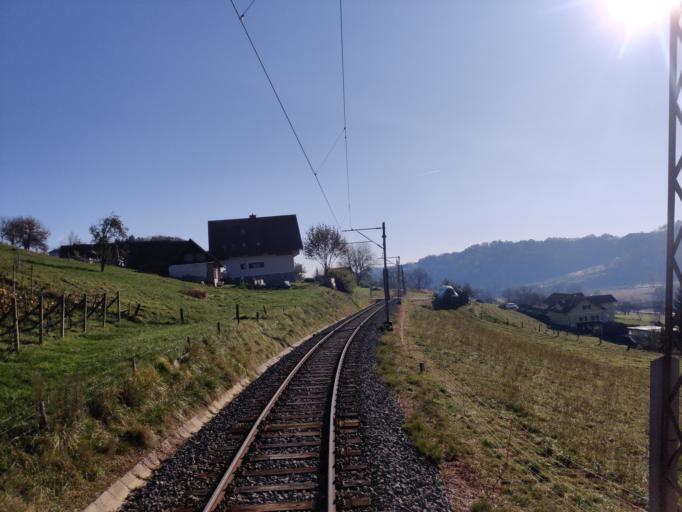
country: AT
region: Styria
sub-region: Politischer Bezirk Suedoststeiermark
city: Trautmannsdorf in Oststeiermark
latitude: 46.8845
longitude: 15.8827
